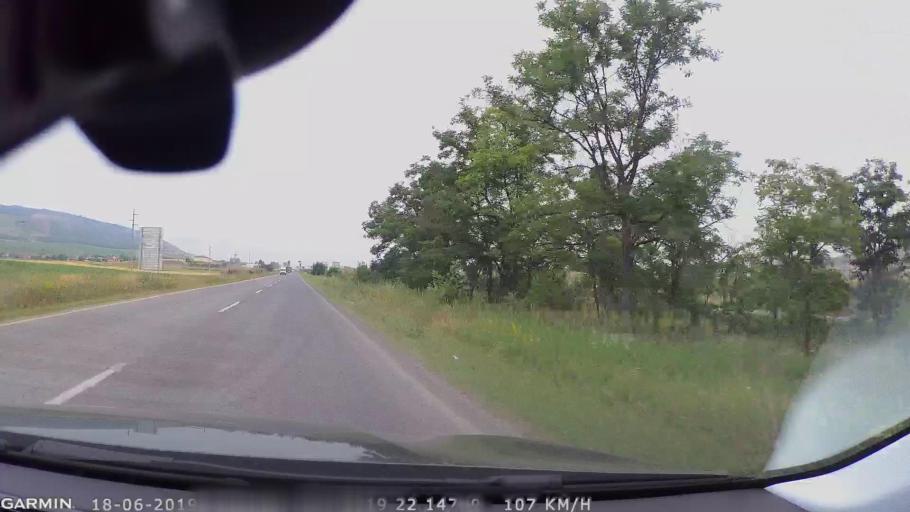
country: MK
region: Stip
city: Shtip
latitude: 41.7706
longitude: 22.1463
